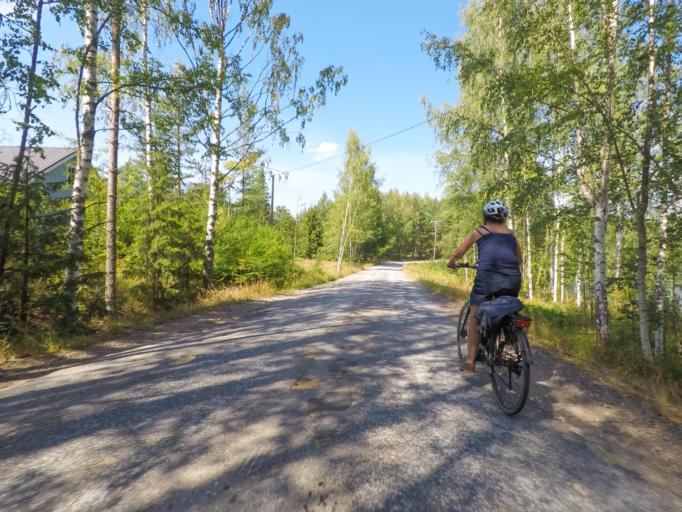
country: FI
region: Southern Savonia
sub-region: Mikkeli
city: Puumala
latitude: 61.4197
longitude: 28.0930
